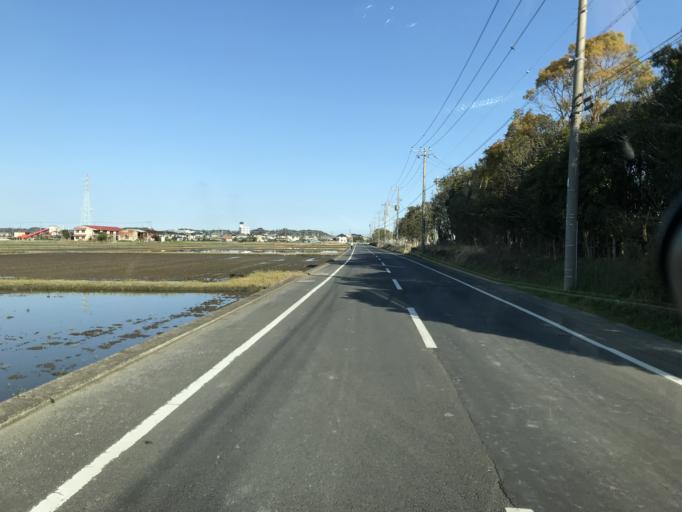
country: JP
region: Chiba
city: Omigawa
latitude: 35.8452
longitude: 140.6137
